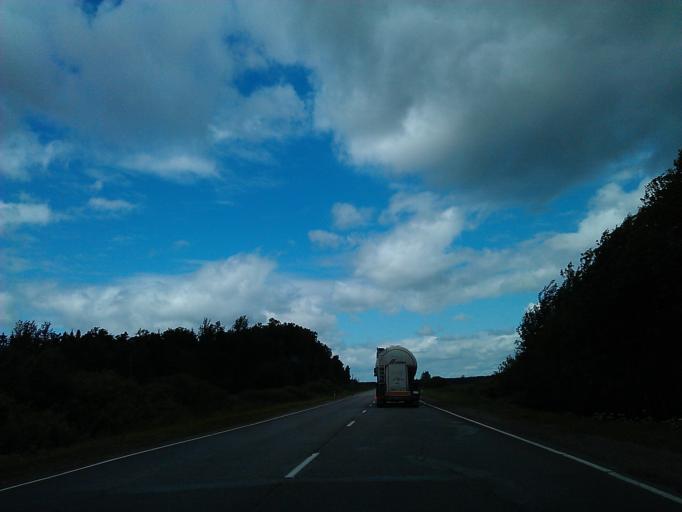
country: LV
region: Tukuma Rajons
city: Tukums
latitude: 56.9360
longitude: 23.1864
